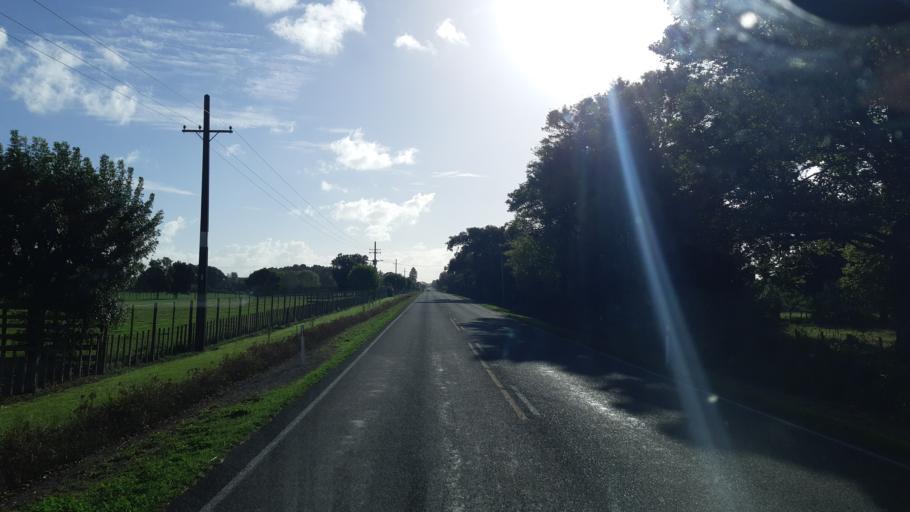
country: NZ
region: Manawatu-Wanganui
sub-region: Wanganui District
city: Wanganui
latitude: -39.9505
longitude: 175.1558
